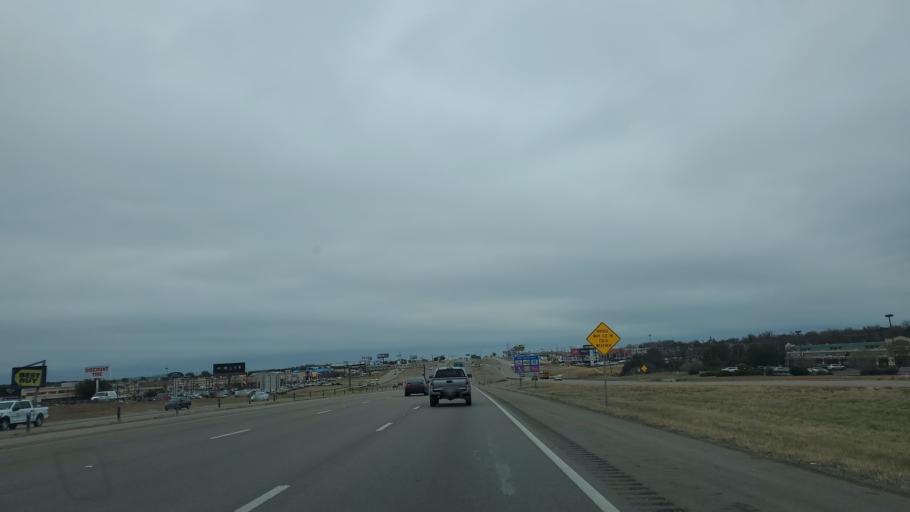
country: US
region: Texas
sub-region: Bell County
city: Killeen
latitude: 31.0860
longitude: -97.7103
